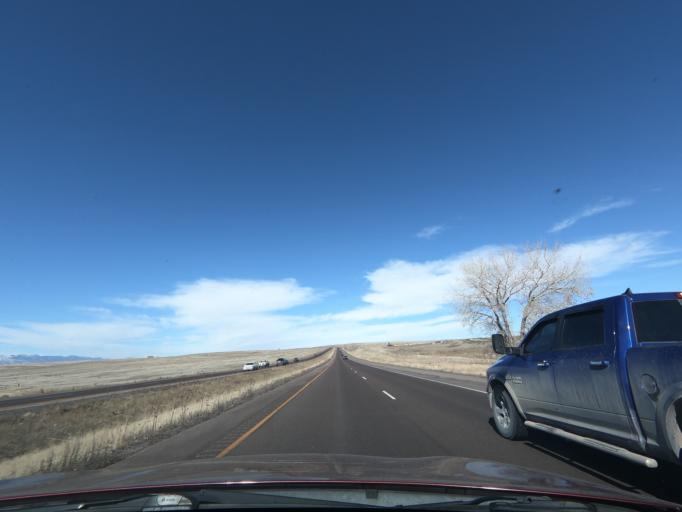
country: US
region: Colorado
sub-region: El Paso County
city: Security-Widefield
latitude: 38.7506
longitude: -104.6827
